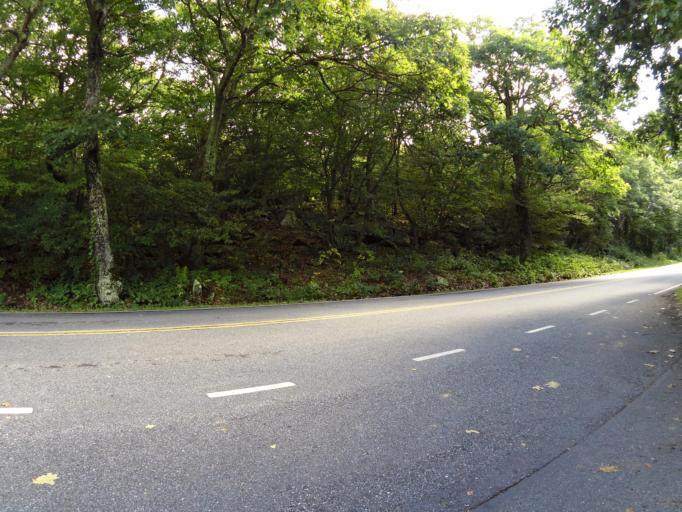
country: US
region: Virginia
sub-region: Page County
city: Stanley
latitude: 38.5618
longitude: -78.3831
